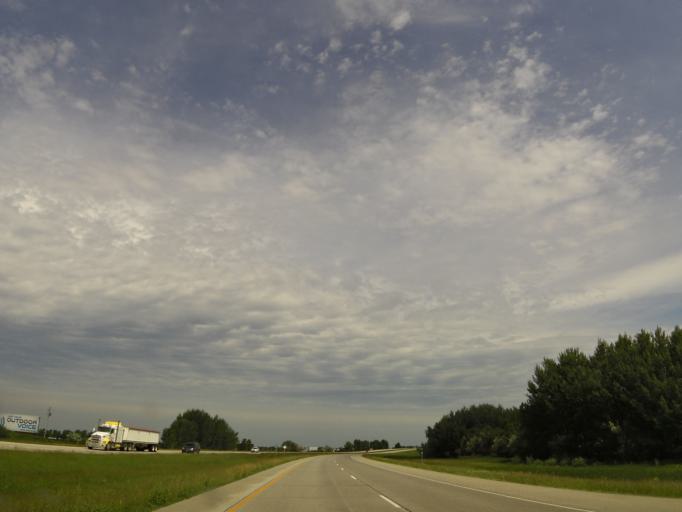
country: US
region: North Dakota
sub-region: Grand Forks County
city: Grand Forks
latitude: 47.9756
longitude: -97.0952
